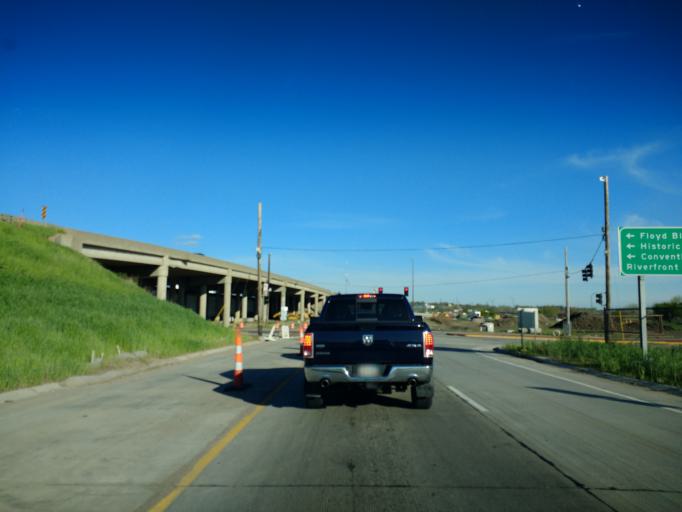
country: US
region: Iowa
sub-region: Woodbury County
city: Sioux City
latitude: 42.4870
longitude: -96.3962
